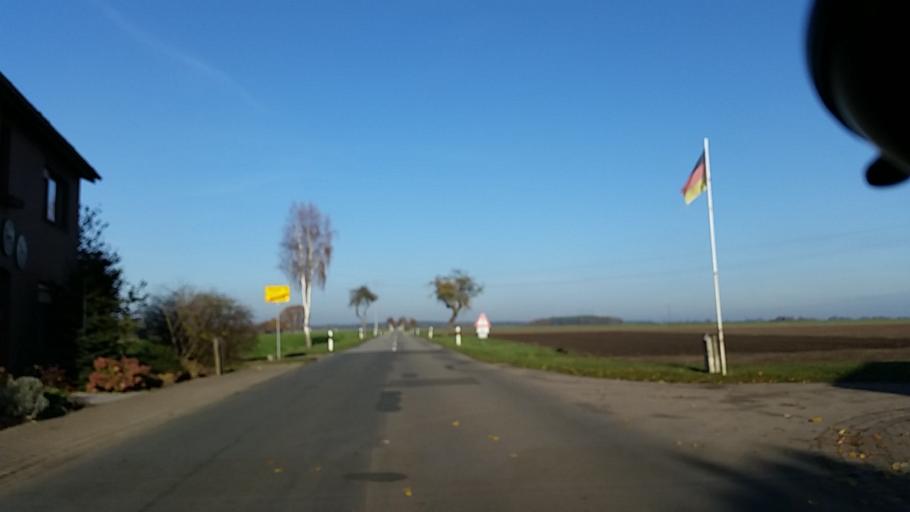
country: DE
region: Lower Saxony
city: Tulau
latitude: 52.5937
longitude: 10.8821
